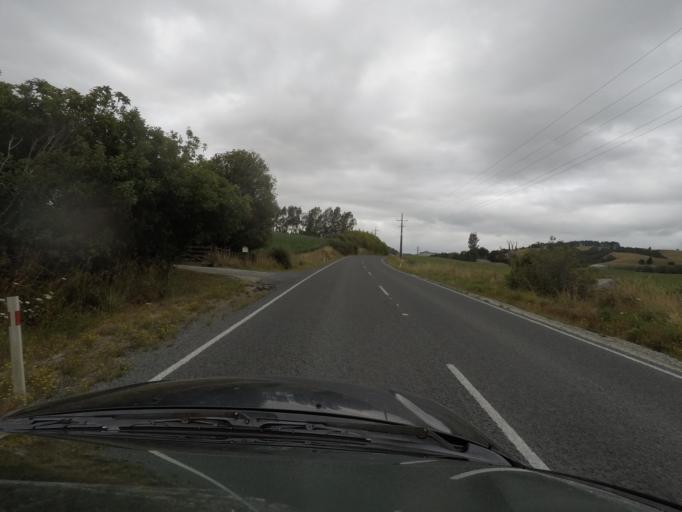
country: NZ
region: Auckland
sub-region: Auckland
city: Wellsford
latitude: -36.2819
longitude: 174.5686
